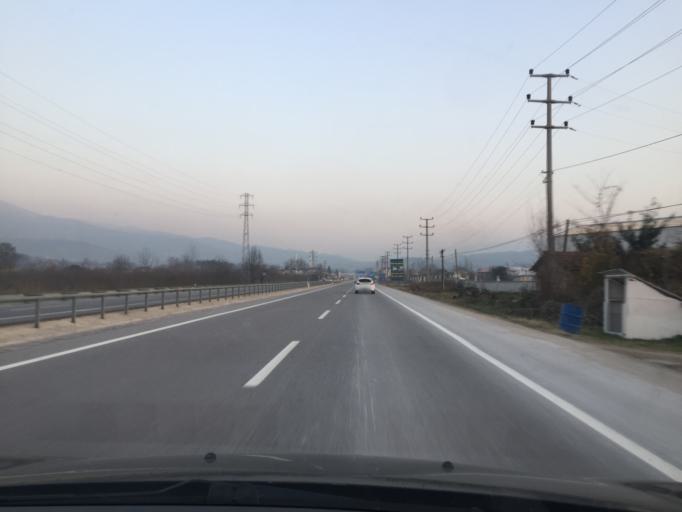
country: TR
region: Sakarya
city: Akyazi
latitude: 40.6381
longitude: 30.6198
